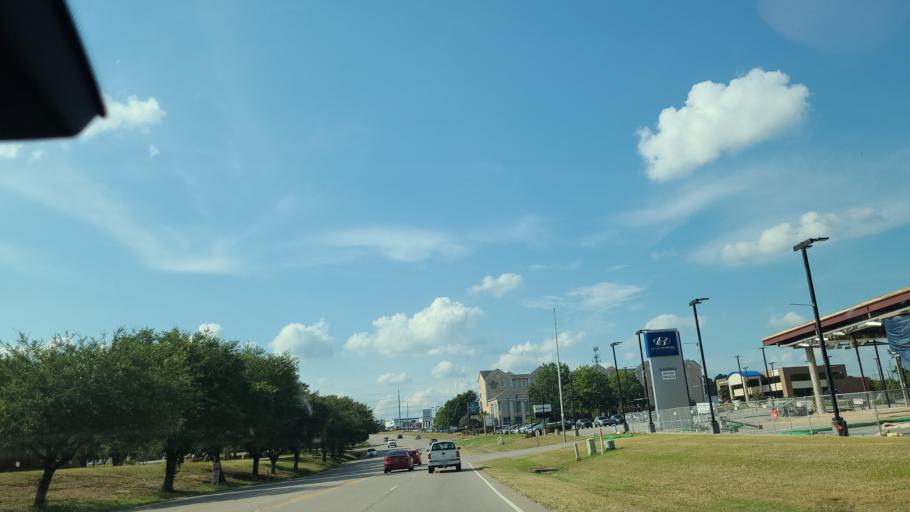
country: US
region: South Carolina
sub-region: Lexington County
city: West Columbia
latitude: 34.0167
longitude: -81.0758
